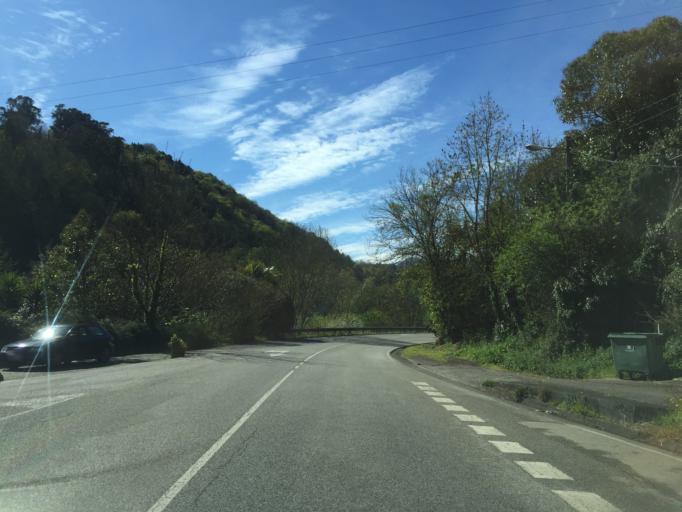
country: ES
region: Asturias
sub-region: Province of Asturias
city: Proaza
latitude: 43.3377
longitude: -5.9856
